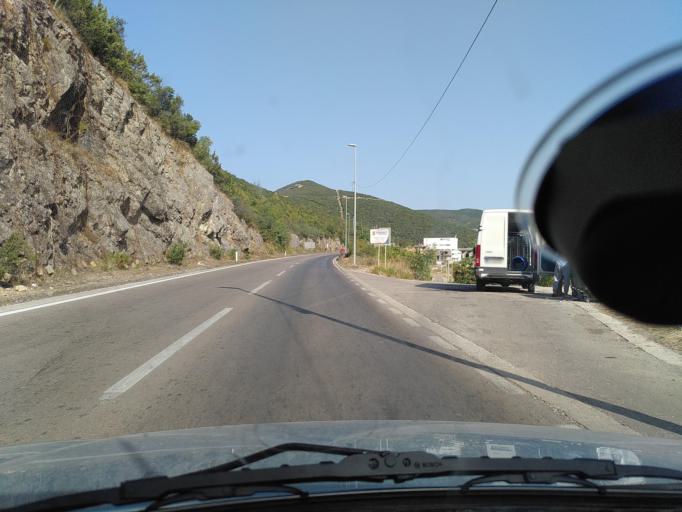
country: ME
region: Ulcinj
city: Ulcinj
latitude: 41.9483
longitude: 19.1983
